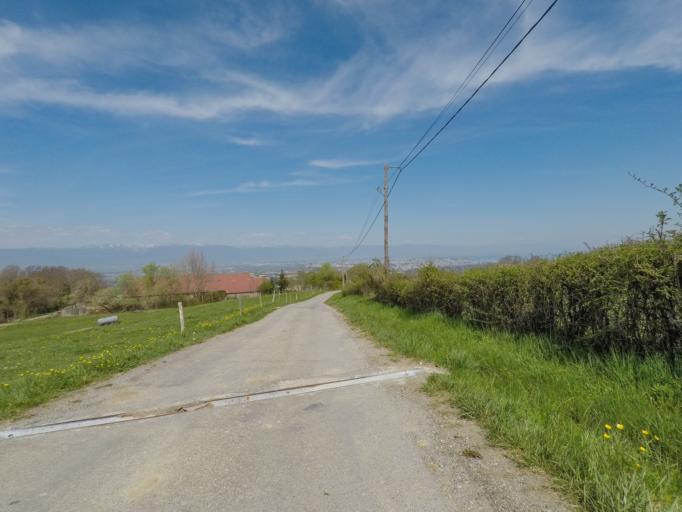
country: FR
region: Rhone-Alpes
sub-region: Departement de la Haute-Savoie
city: Archamps
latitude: 46.1195
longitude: 6.1383
